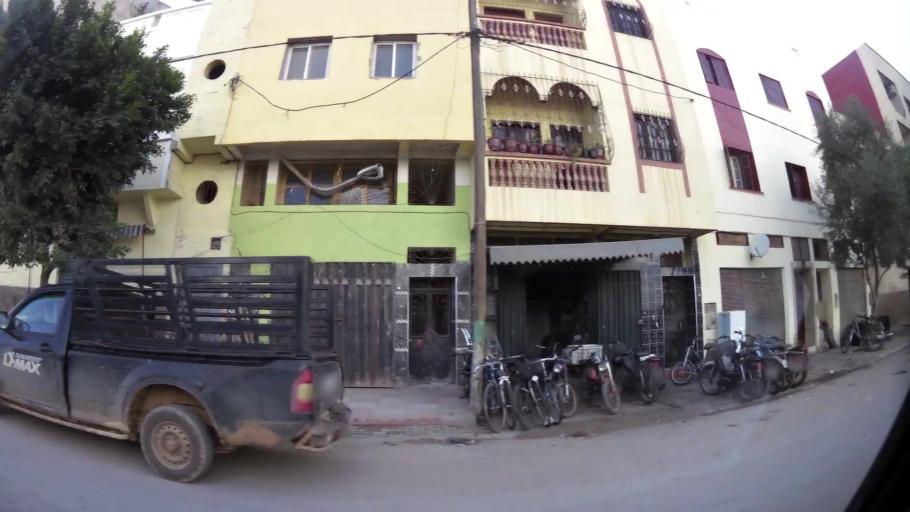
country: MA
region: Chaouia-Ouardigha
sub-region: Settat Province
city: Settat
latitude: 33.0085
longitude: -7.6227
